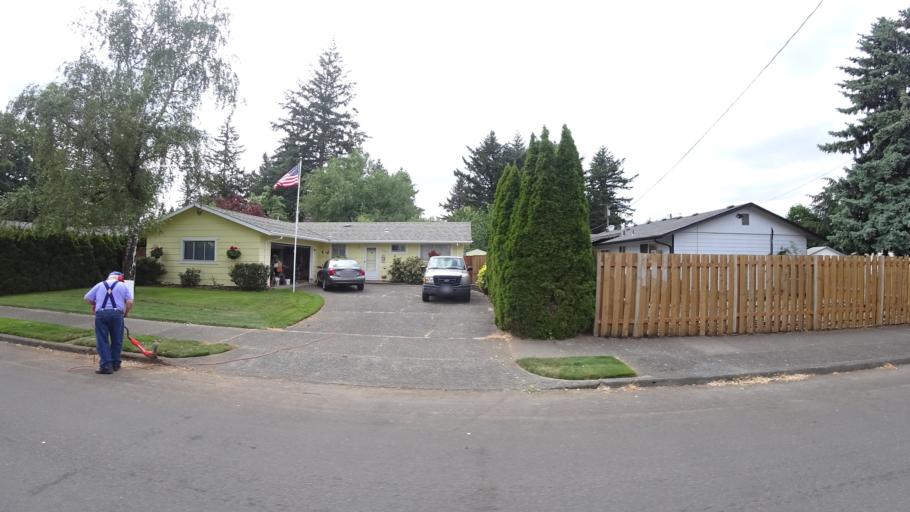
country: US
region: Oregon
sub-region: Multnomah County
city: Fairview
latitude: 45.5165
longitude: -122.4828
